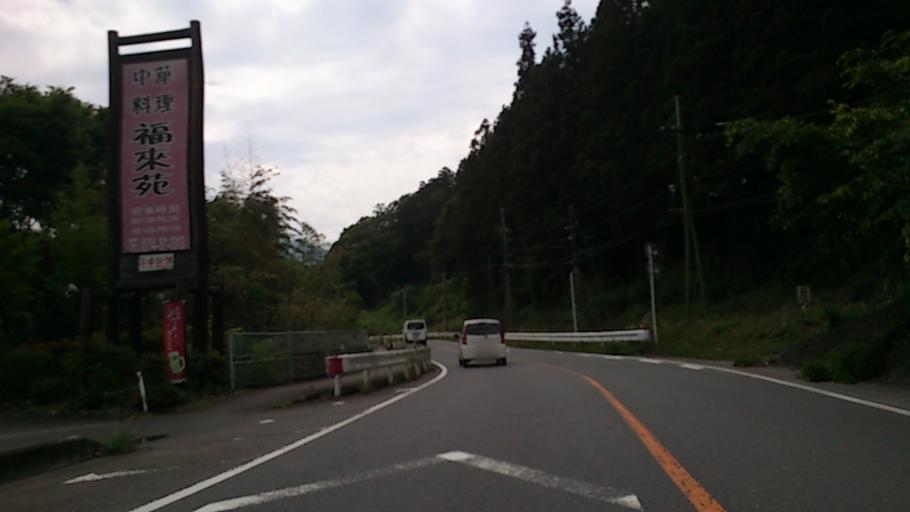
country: JP
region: Gunma
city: Tomioka
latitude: 36.2125
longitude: 138.8002
